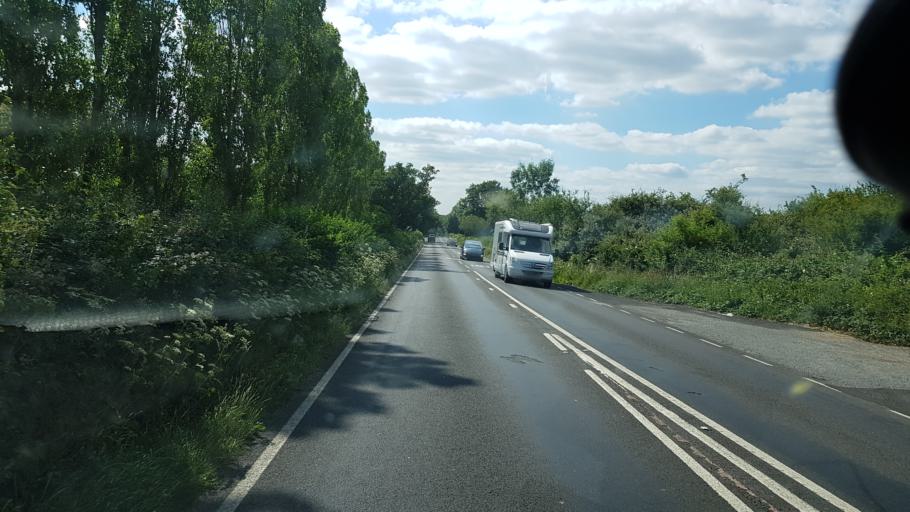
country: GB
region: England
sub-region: West Sussex
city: Partridge Green
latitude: 50.9893
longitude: -0.3164
